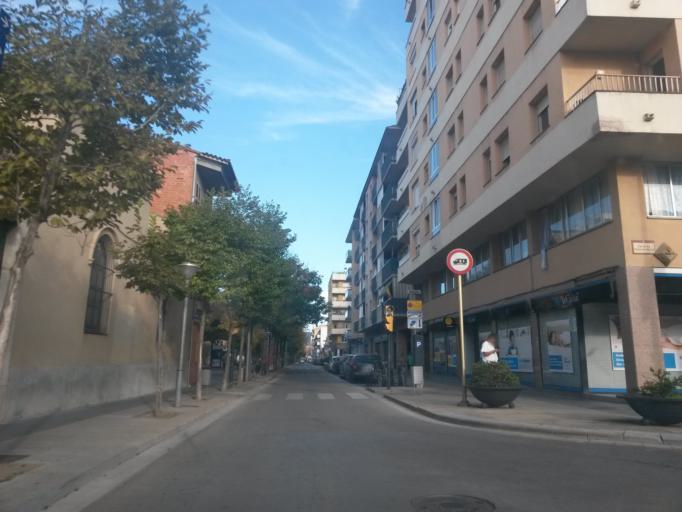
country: ES
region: Catalonia
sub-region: Provincia de Girona
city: Salt
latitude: 41.9752
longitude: 2.7913
